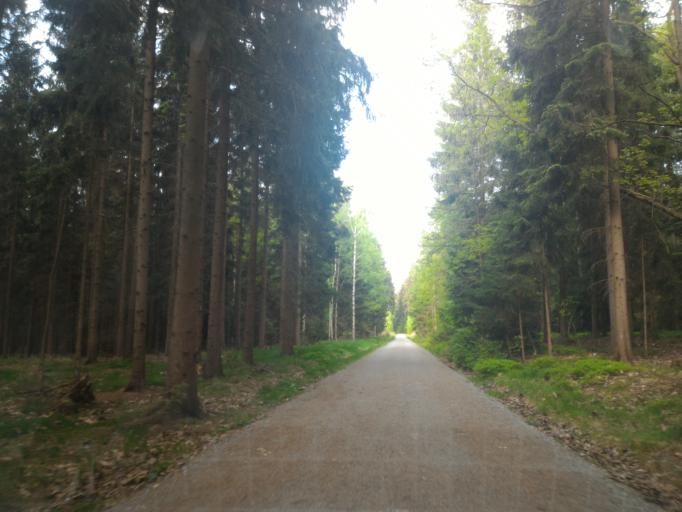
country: DE
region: Saxony
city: Neugersdorf
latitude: 50.9580
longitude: 14.6132
